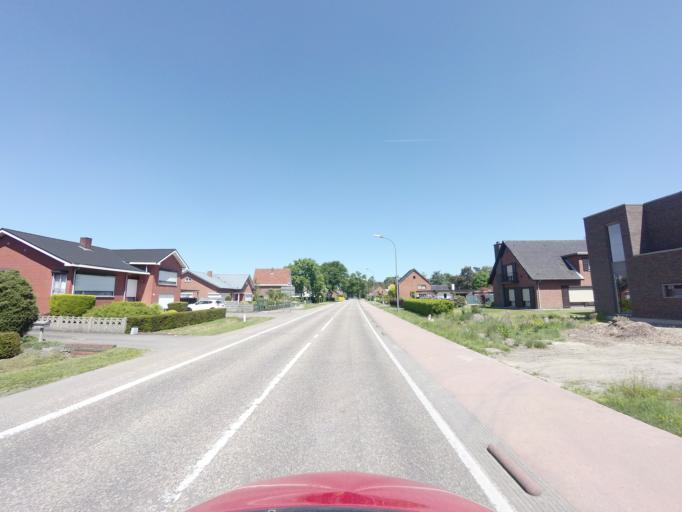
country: BE
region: Flanders
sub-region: Provincie Limburg
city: Lommel
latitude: 51.2559
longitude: 5.3127
